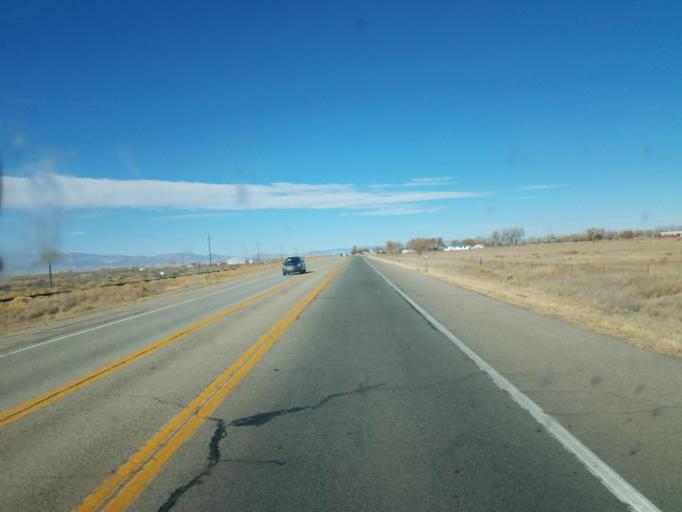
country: US
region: Colorado
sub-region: Alamosa County
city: Alamosa
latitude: 37.5034
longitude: -105.9611
